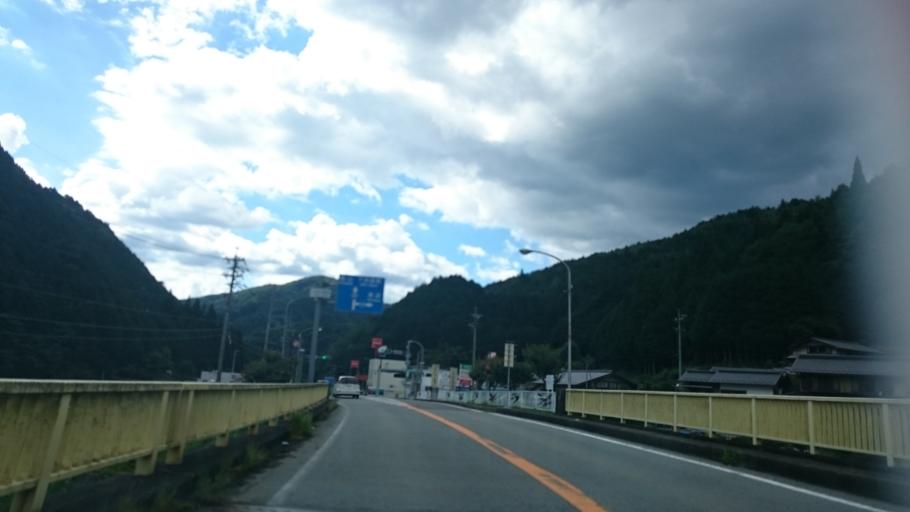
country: JP
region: Gifu
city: Gujo
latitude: 35.7679
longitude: 137.2840
